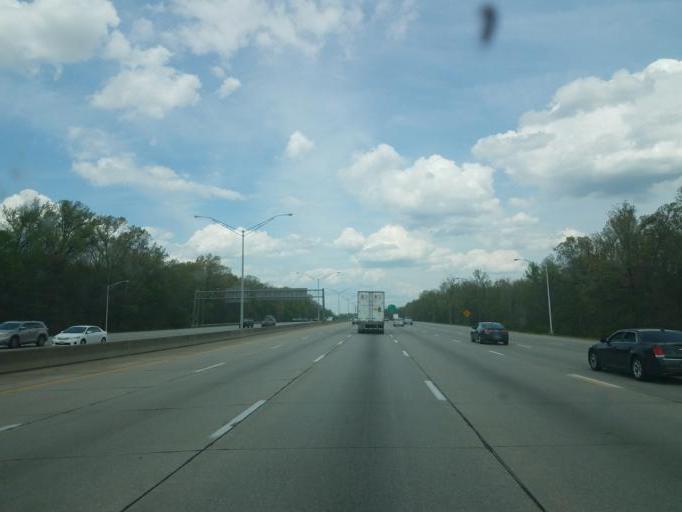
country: US
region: Kentucky
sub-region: Jefferson County
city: Heritage Creek
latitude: 38.1203
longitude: -85.7018
